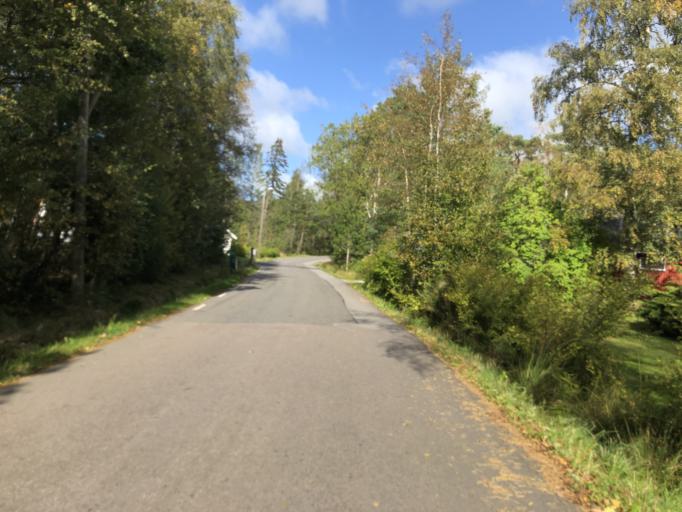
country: SE
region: Vaestra Goetaland
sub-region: Goteborg
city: Torslanda
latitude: 57.7370
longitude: 11.8389
